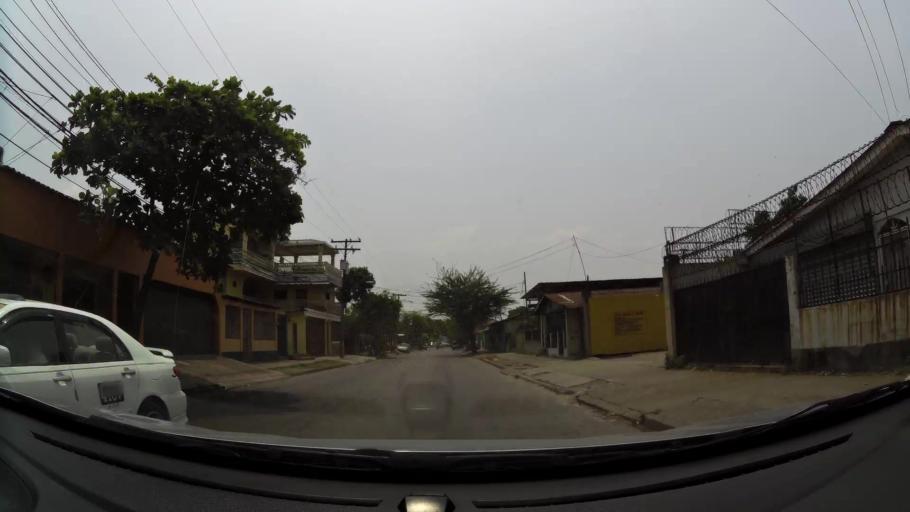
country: HN
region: Cortes
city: San Pedro Sula
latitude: 15.4903
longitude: -88.0132
